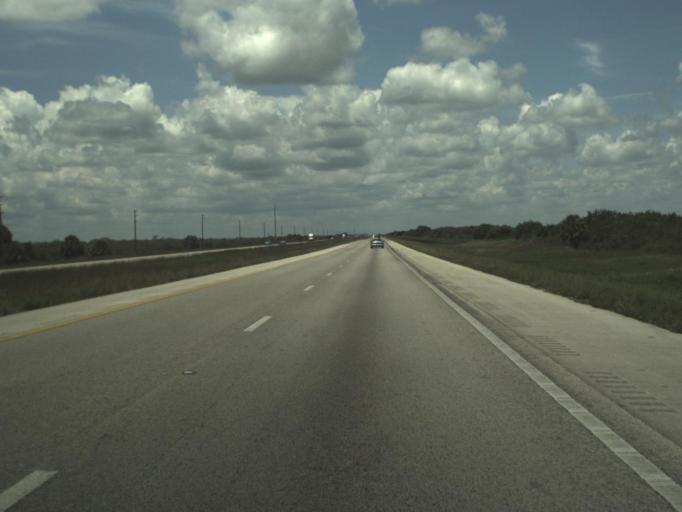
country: US
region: Florida
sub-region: Broward County
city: Weston
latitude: 26.1568
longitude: -80.7655
